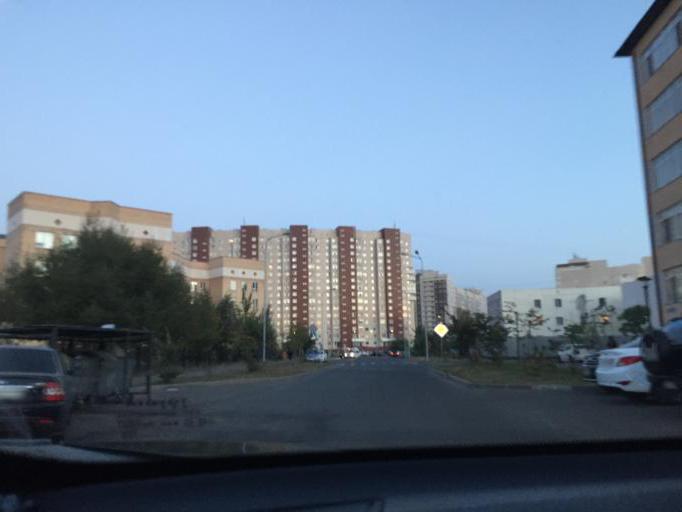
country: KZ
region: Astana Qalasy
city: Astana
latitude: 51.1434
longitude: 71.4797
